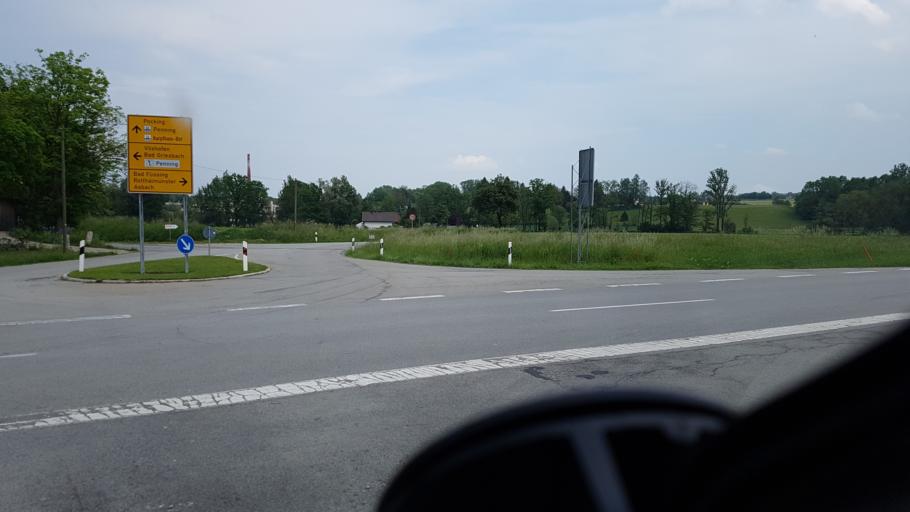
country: DE
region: Bavaria
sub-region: Lower Bavaria
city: Bayerbach
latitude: 48.4065
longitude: 13.1790
